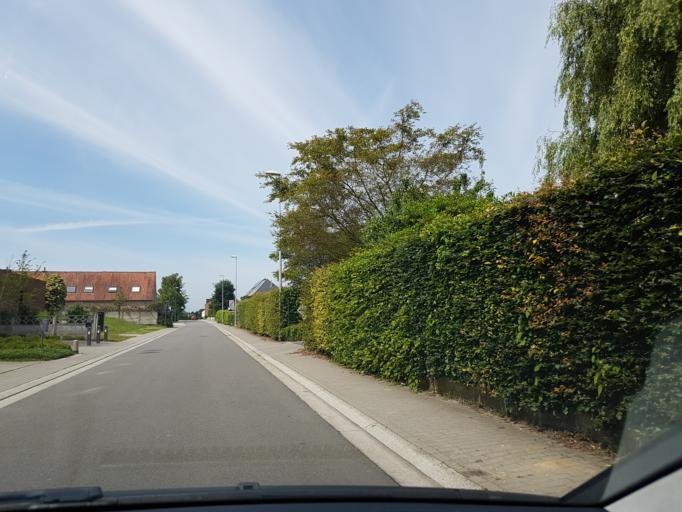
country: BE
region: Flanders
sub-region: Provincie Oost-Vlaanderen
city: Denderleeuw
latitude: 50.9219
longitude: 4.0921
